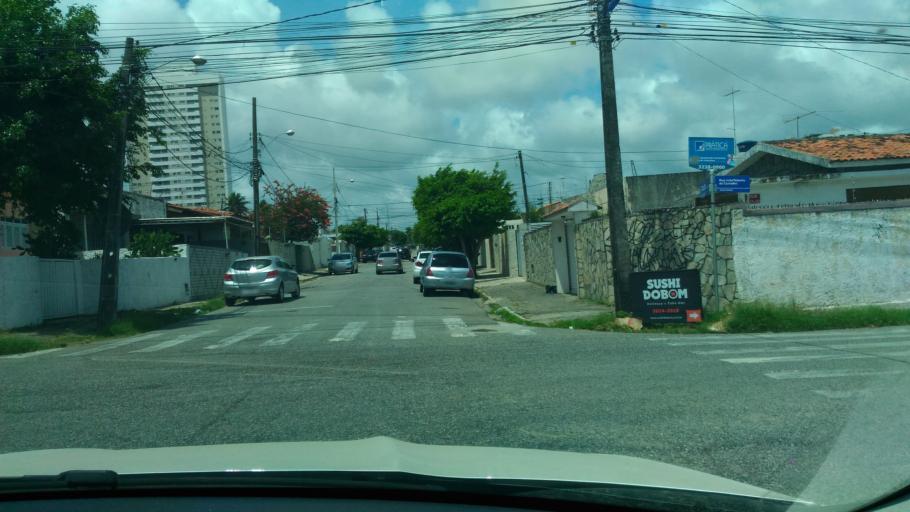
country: BR
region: Paraiba
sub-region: Joao Pessoa
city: Joao Pessoa
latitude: -7.1175
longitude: -34.8456
